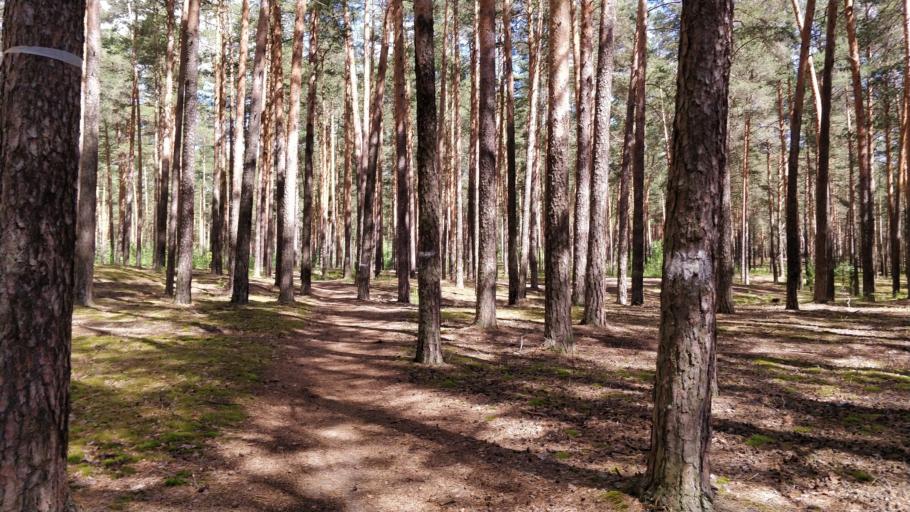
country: RU
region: Perm
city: Perm
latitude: 58.0629
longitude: 56.3019
